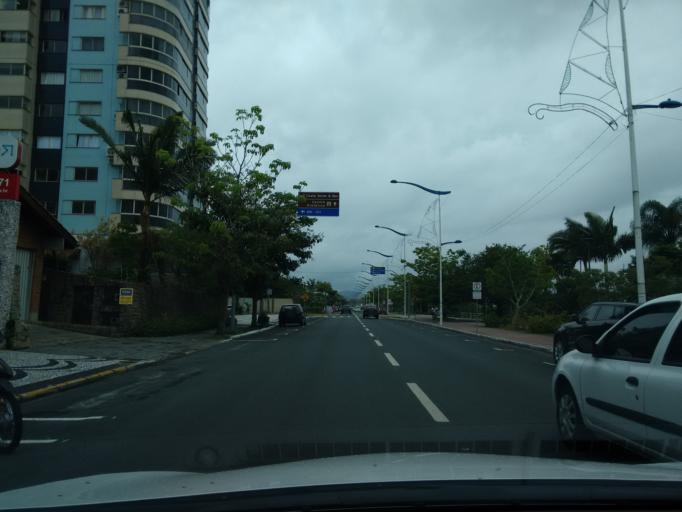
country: BR
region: Santa Catarina
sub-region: Itajai
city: Itajai
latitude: -26.9145
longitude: -48.6533
